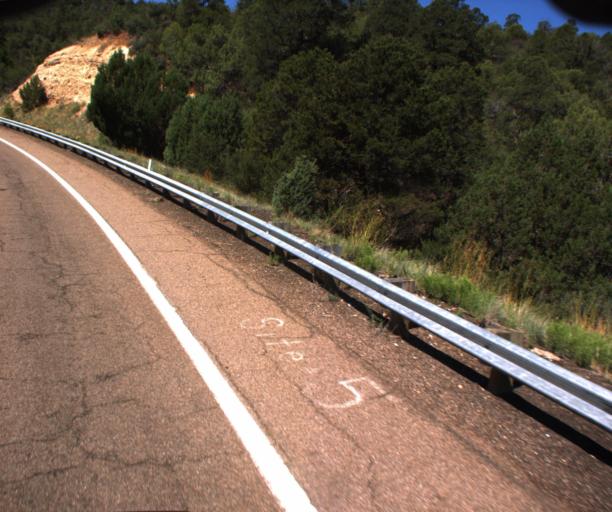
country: US
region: Arizona
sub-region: Navajo County
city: Cibecue
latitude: 33.9291
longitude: -110.3578
